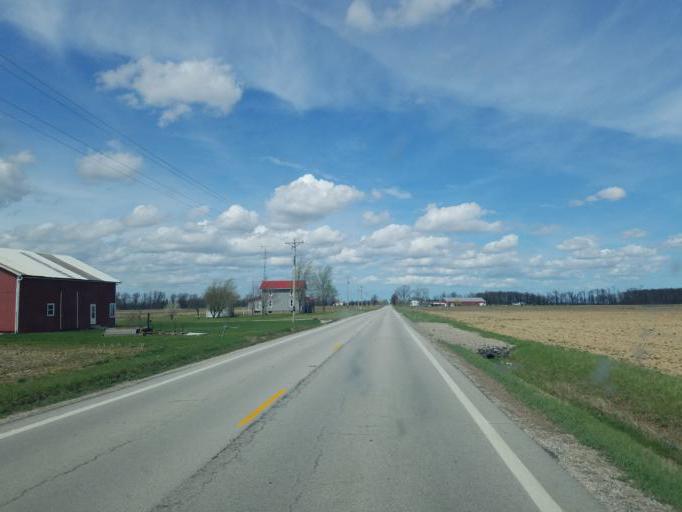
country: US
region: Ohio
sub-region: Huron County
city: Bellevue
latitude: 41.2065
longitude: -82.8217
